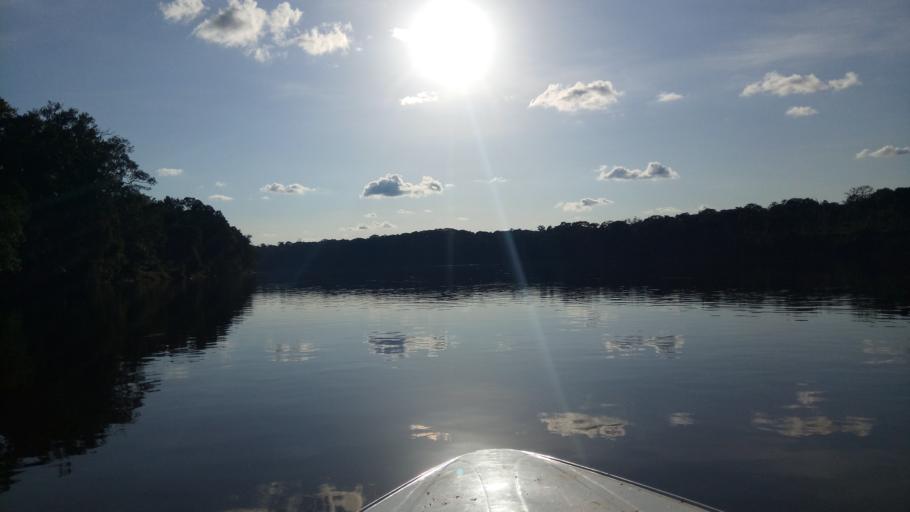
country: CD
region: Eastern Province
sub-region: Sous-Region de la Tshopo
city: Yangambi
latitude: 0.2553
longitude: 24.0596
